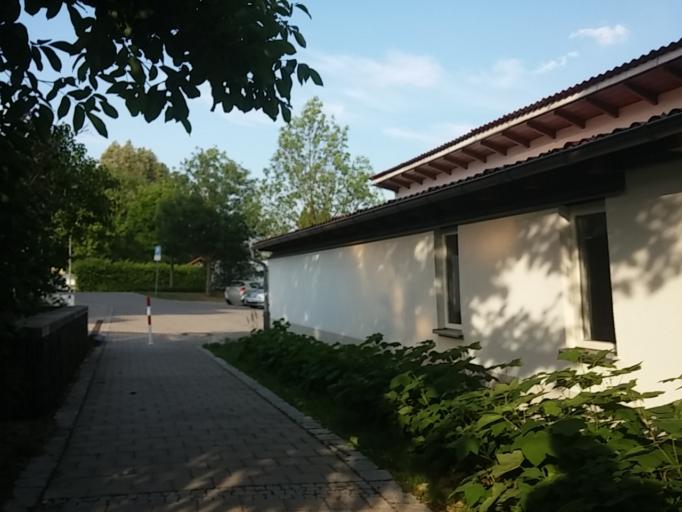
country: DE
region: Bavaria
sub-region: Upper Bavaria
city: Vaterstetten
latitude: 48.1104
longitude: 11.7785
